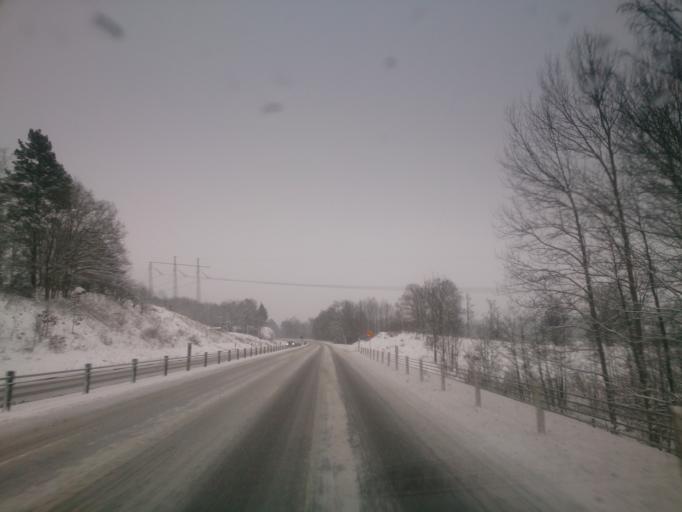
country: SE
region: OEstergoetland
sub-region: Finspangs Kommun
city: Finspang
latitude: 58.7022
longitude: 15.8834
